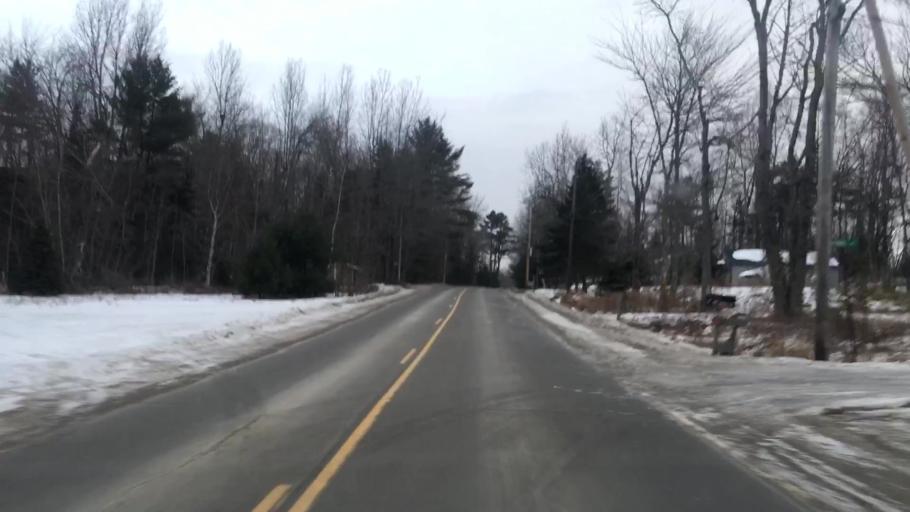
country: US
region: Maine
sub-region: Hancock County
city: Ellsworth
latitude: 44.6079
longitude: -68.3926
